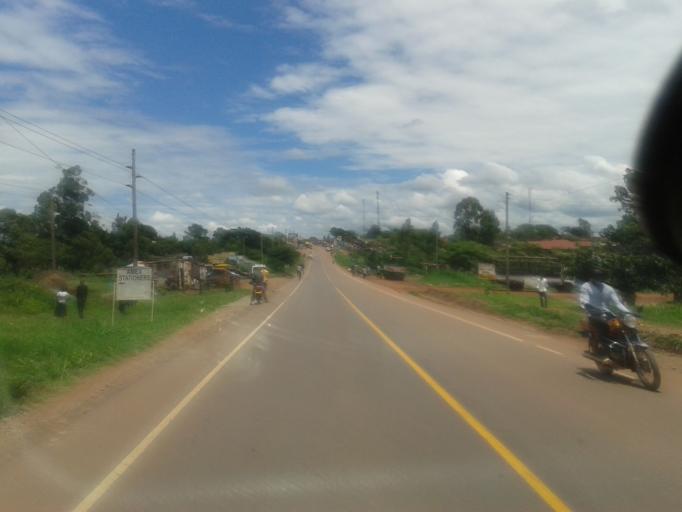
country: UG
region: Western Region
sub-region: Kiryandongo District
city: Kiryandongo
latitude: 1.8130
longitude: 32.0135
